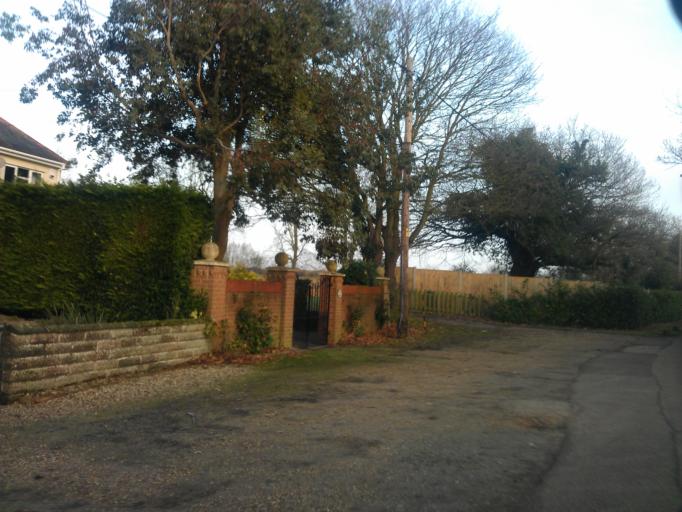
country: GB
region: England
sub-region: Essex
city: Wivenhoe
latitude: 51.8623
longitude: 0.9753
